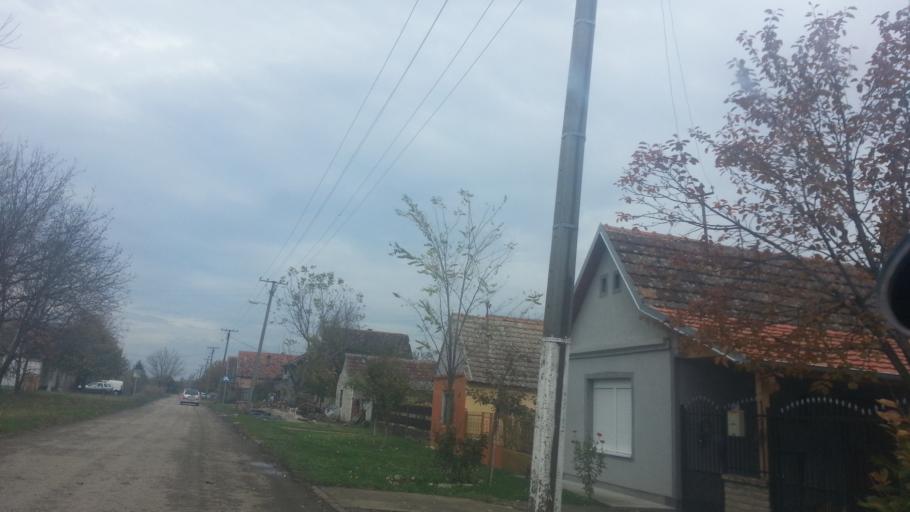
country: RS
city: Golubinci
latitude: 44.9828
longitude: 20.0806
